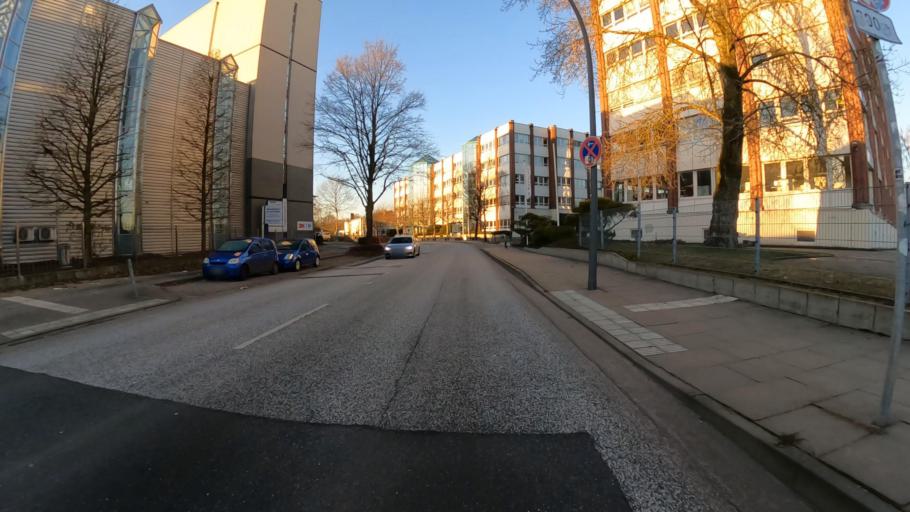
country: DE
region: Hamburg
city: Eidelstedt
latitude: 53.5964
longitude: 9.9024
